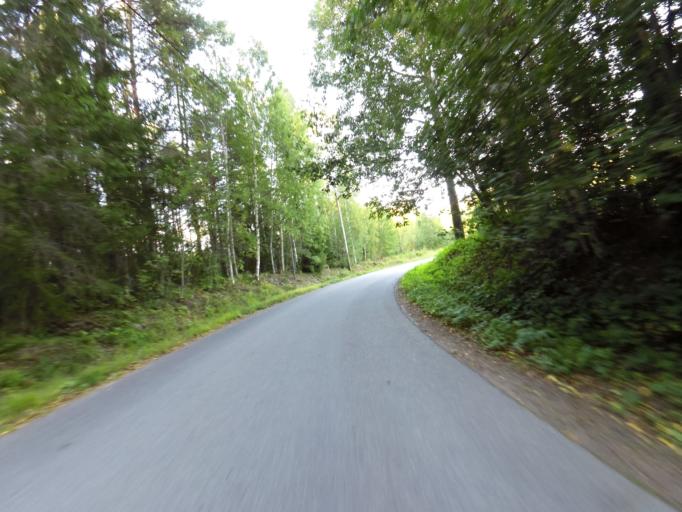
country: SE
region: Gaevleborg
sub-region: Gavle Kommun
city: Gavle
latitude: 60.7188
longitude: 17.1476
